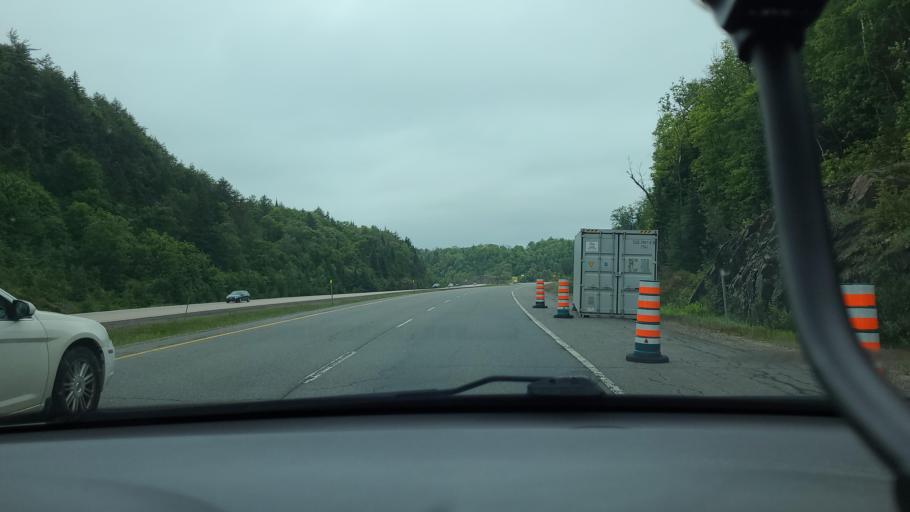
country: CA
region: Quebec
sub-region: Laurentides
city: Mont-Tremblant
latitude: 46.1505
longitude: -74.6623
